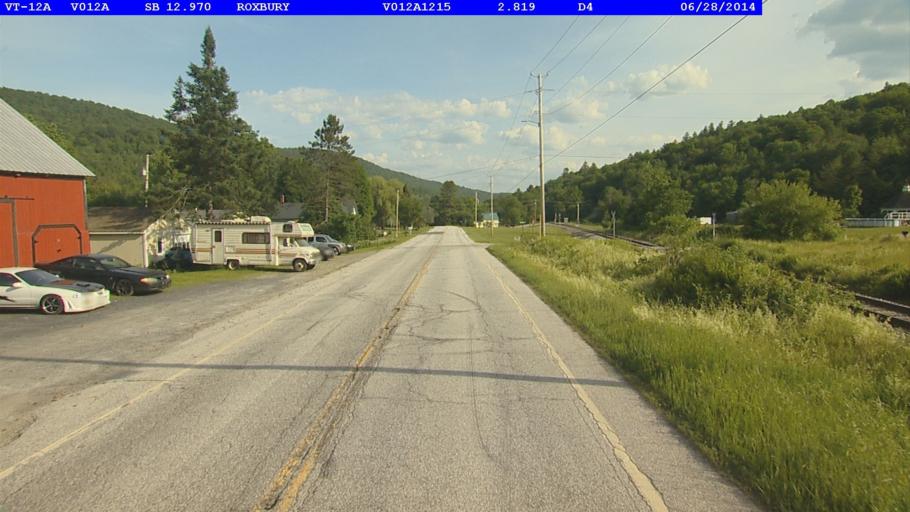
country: US
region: Vermont
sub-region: Washington County
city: Northfield
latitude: 44.0689
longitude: -72.7455
